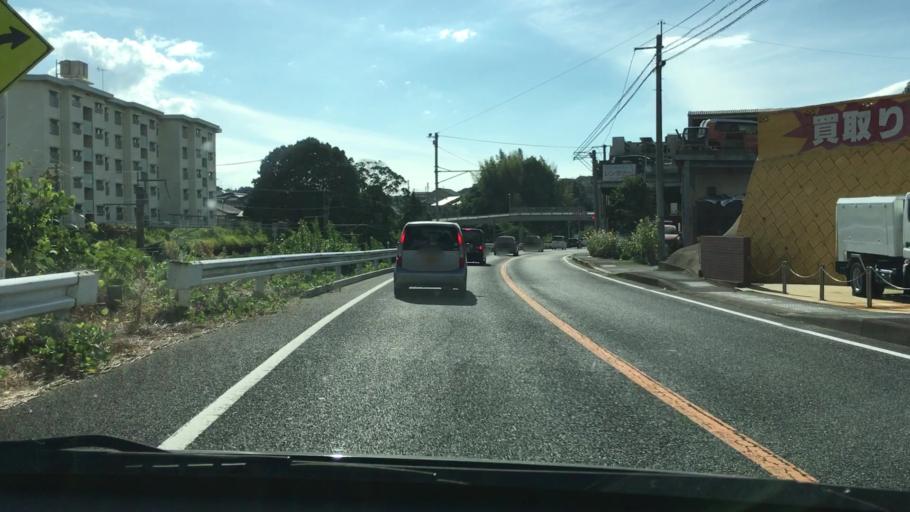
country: JP
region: Nagasaki
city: Sasebo
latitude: 33.1441
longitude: 129.8111
